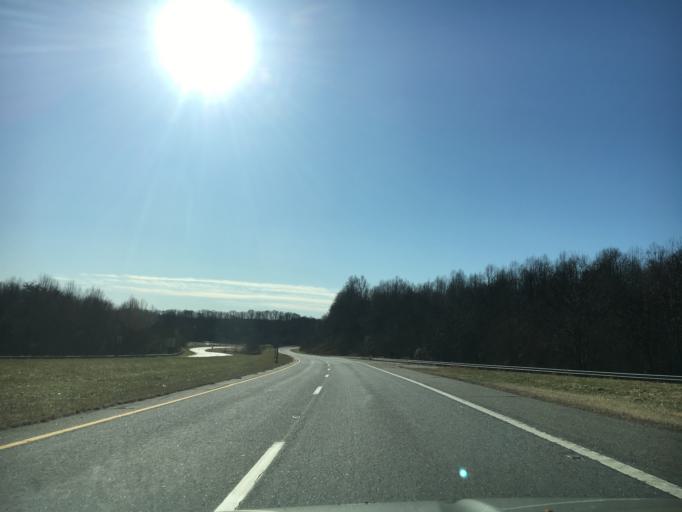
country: US
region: Virginia
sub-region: Henry County
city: Chatmoss
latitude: 36.6446
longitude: -79.8233
